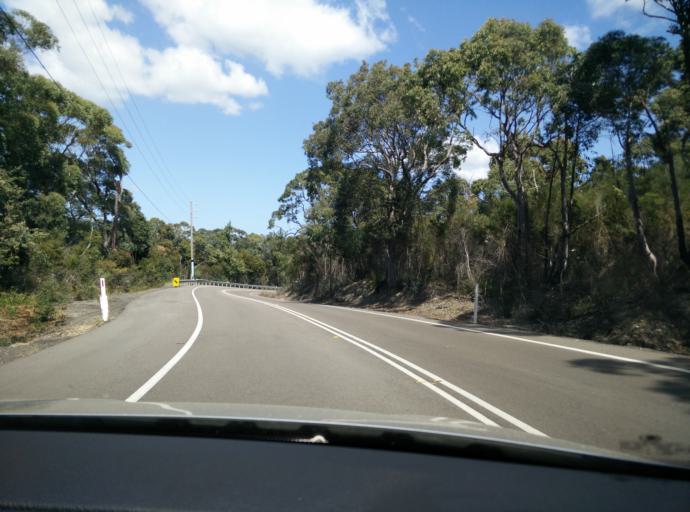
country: AU
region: New South Wales
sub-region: Gosford Shire
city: Blackwall
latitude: -33.4867
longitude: 151.3039
